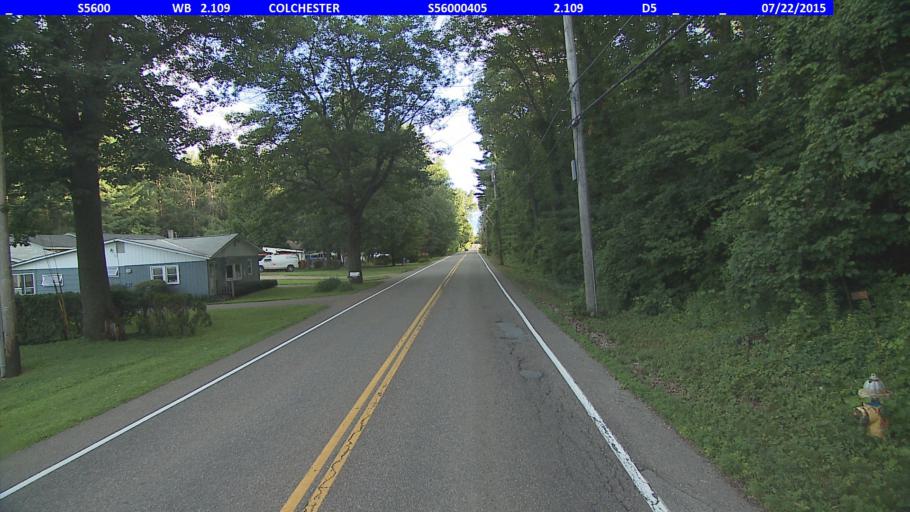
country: US
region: Vermont
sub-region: Chittenden County
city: Winooski
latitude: 44.5504
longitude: -73.2346
